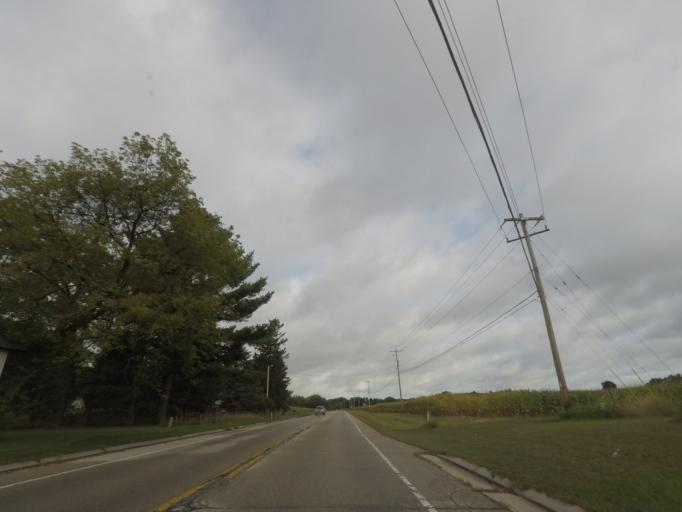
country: US
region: Wisconsin
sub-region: Waukesha County
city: Dousman
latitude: 43.0234
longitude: -88.5013
